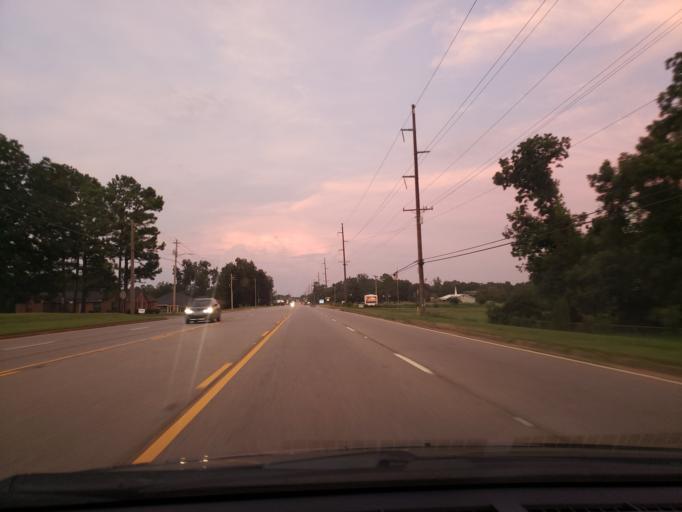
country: US
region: Georgia
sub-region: Dougherty County
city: Albany
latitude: 31.5856
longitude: -84.2317
